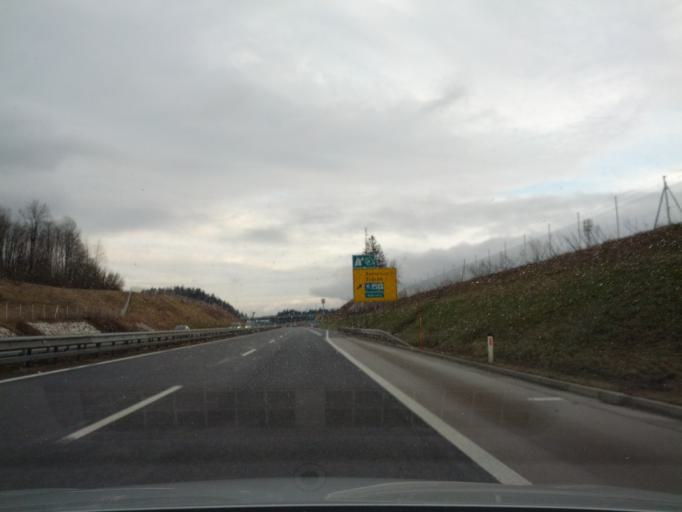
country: SI
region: Radovljica
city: Radovljica
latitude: 46.3445
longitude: 14.1845
